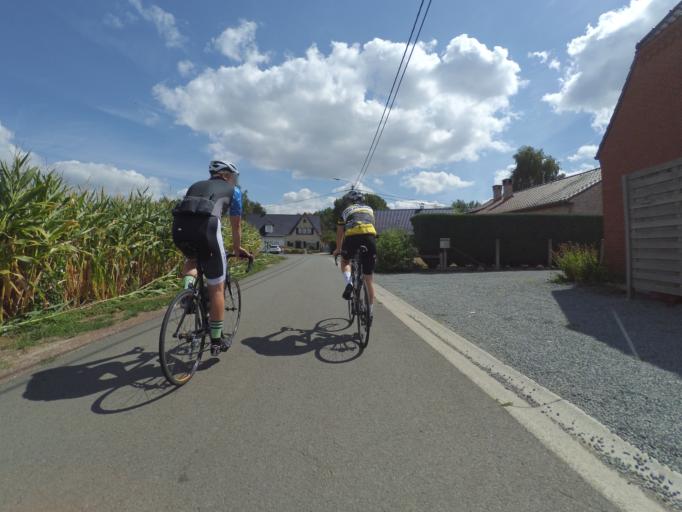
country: BE
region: Wallonia
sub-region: Province du Hainaut
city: Ellezelles
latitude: 50.7984
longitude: 3.6990
